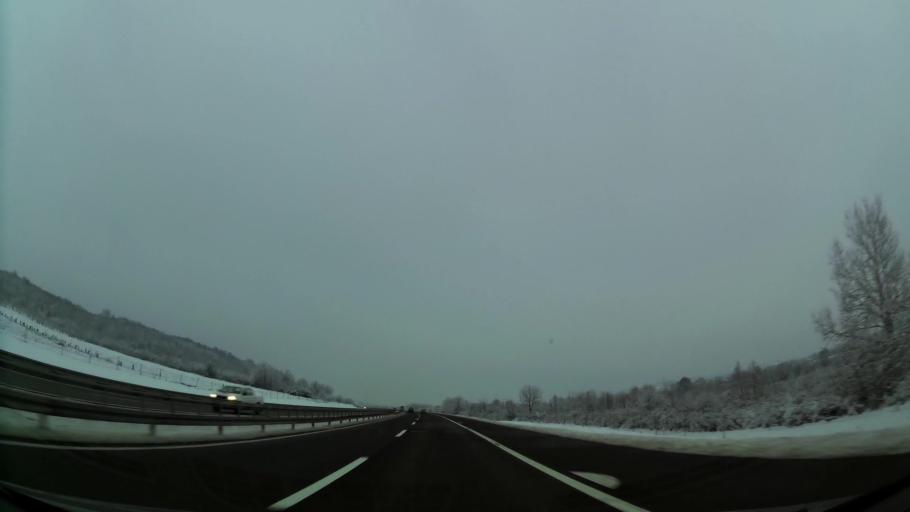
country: RS
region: Central Serbia
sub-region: Belgrade
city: Grocka
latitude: 44.5797
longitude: 20.7800
